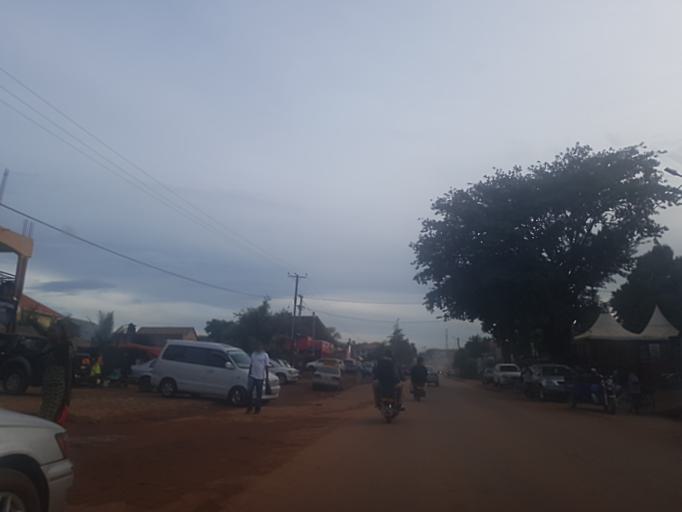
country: UG
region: Central Region
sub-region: Wakiso District
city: Bweyogerere
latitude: 0.3833
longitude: 32.6499
